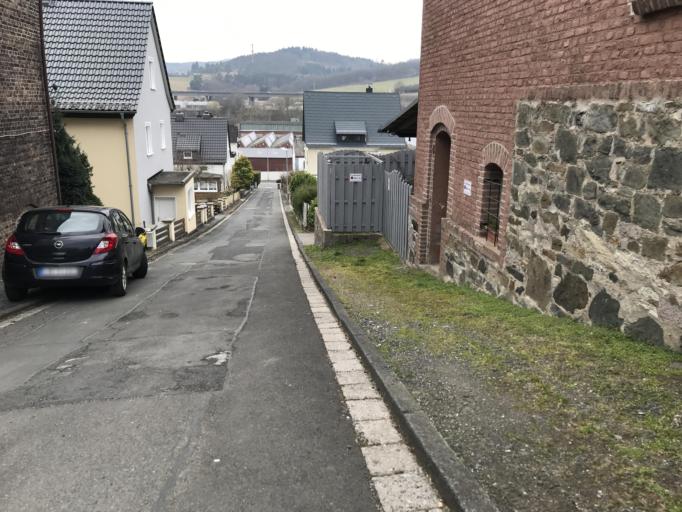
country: DE
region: Hesse
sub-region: Regierungsbezirk Giessen
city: Sinn
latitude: 50.6557
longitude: 8.3289
